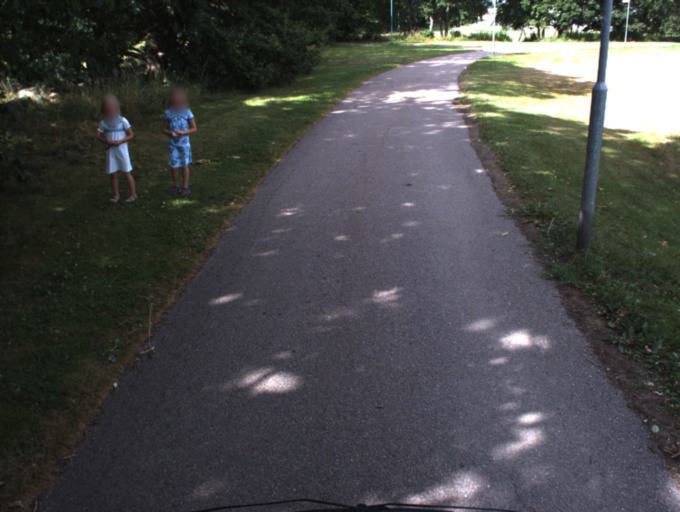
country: SE
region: Skane
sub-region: Helsingborg
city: Barslov
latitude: 56.0142
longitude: 12.8004
